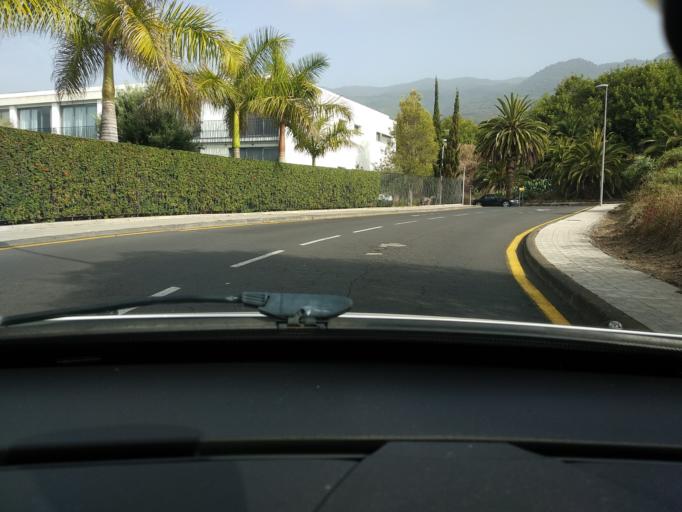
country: ES
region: Canary Islands
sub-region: Provincia de Santa Cruz de Tenerife
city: Santa Ursula
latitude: 28.4285
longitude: -16.4911
